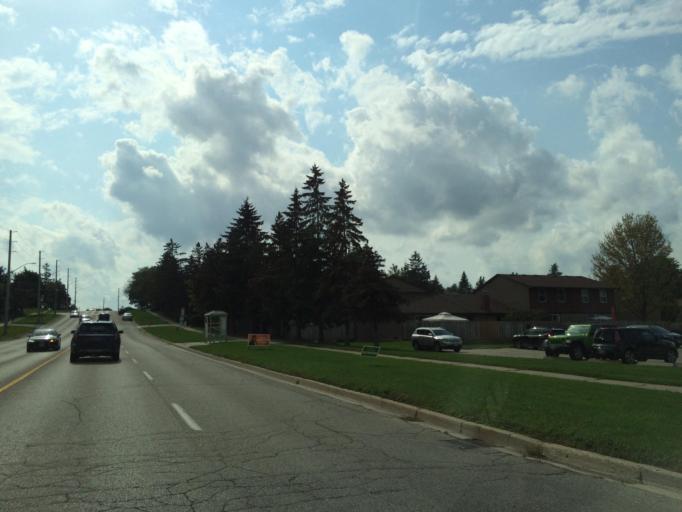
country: CA
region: Ontario
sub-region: Wellington County
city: Guelph
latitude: 43.5334
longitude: -80.2873
